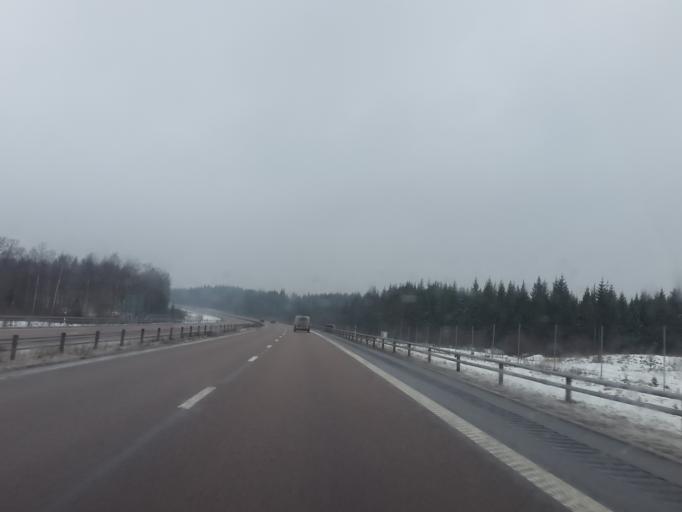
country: SE
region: Vaestra Goetaland
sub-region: Boras Kommun
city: Dalsjofors
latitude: 57.8088
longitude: 13.2000
